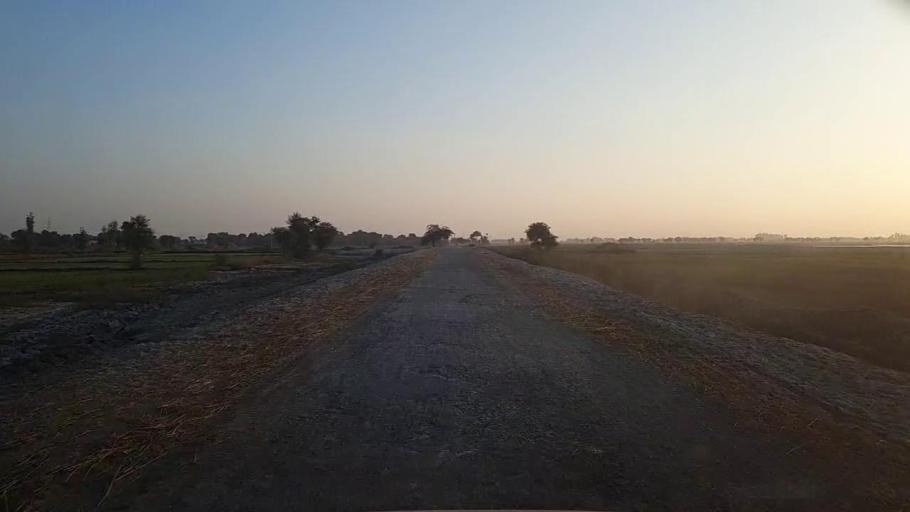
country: PK
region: Sindh
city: Khairpur Nathan Shah
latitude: 27.1755
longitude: 67.7339
